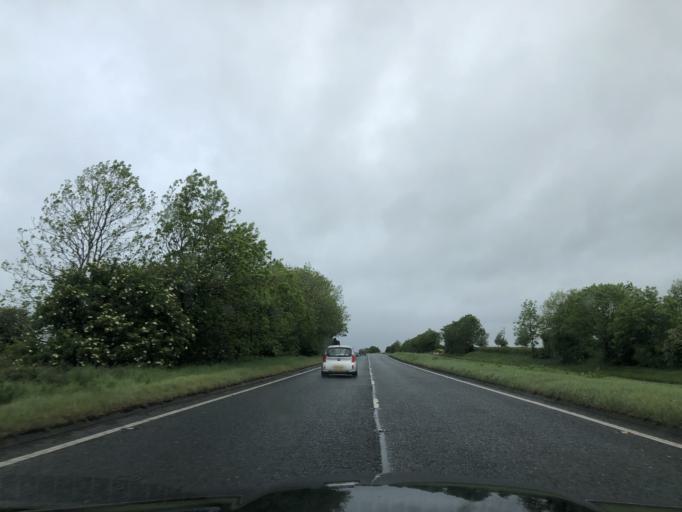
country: GB
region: Northern Ireland
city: Connor
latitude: 54.8002
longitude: -6.2569
